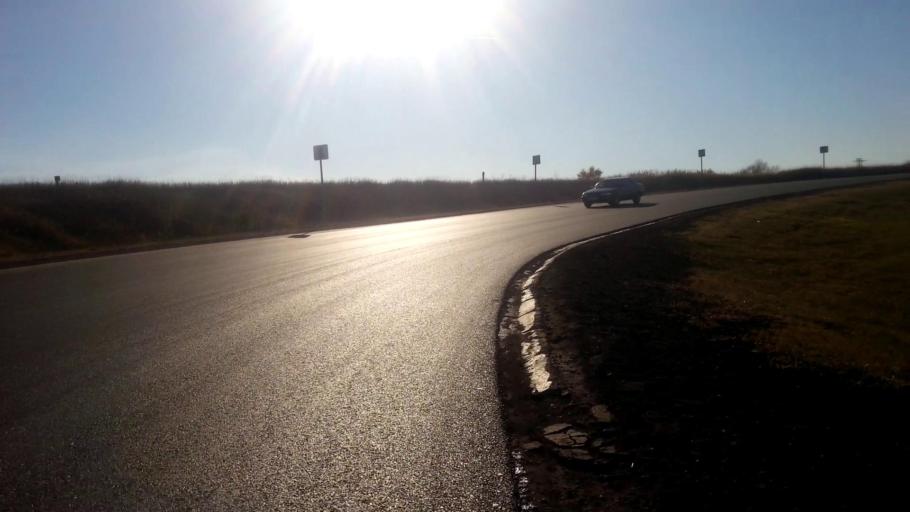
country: RU
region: Altai Krai
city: Novoaltaysk
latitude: 53.3701
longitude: 83.9568
